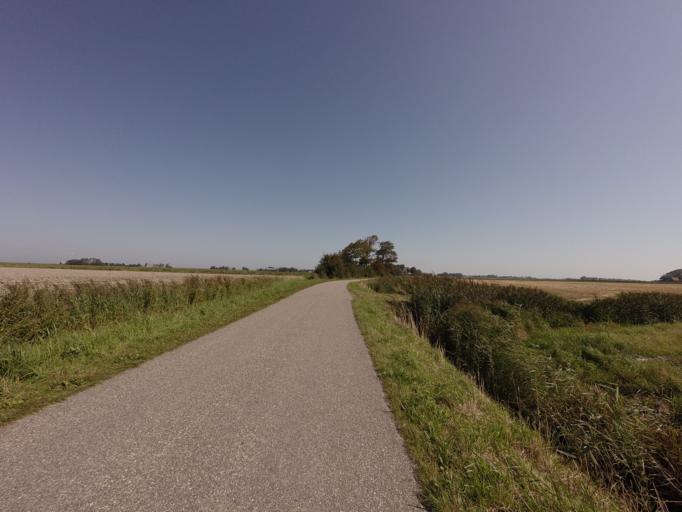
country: NL
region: Friesland
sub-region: Gemeente Dongeradeel
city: Holwerd
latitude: 53.3690
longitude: 5.9175
